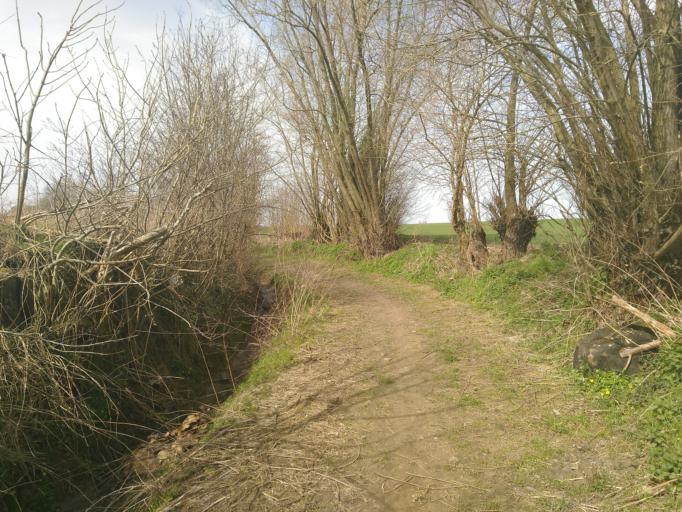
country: BE
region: Wallonia
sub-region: Province du Brabant Wallon
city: Chaumont-Gistoux
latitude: 50.6788
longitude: 4.7409
